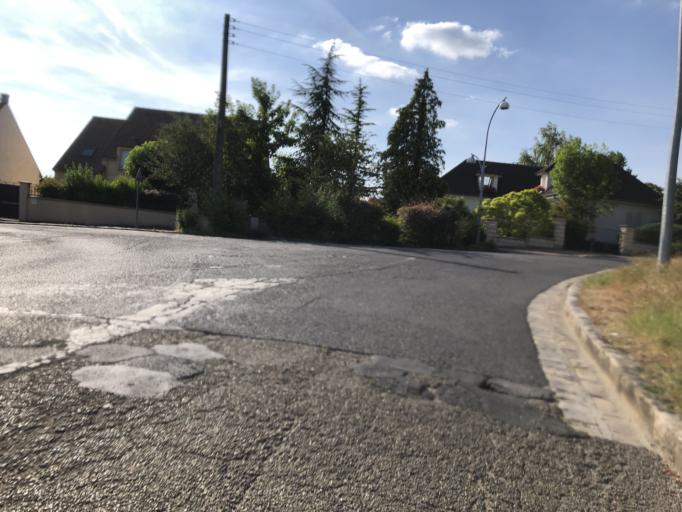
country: FR
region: Ile-de-France
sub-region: Departement des Yvelines
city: Triel-sur-Seine
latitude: 48.9783
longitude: 2.0136
